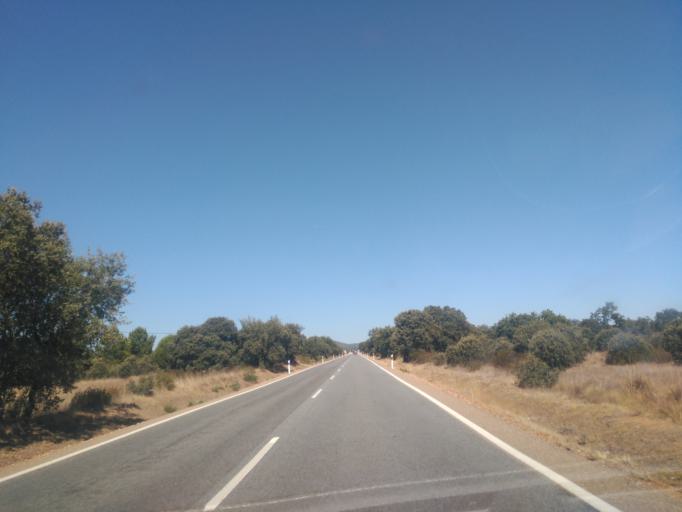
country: ES
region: Castille and Leon
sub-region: Provincia de Zamora
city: Tabara
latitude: 41.8123
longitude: -5.9368
